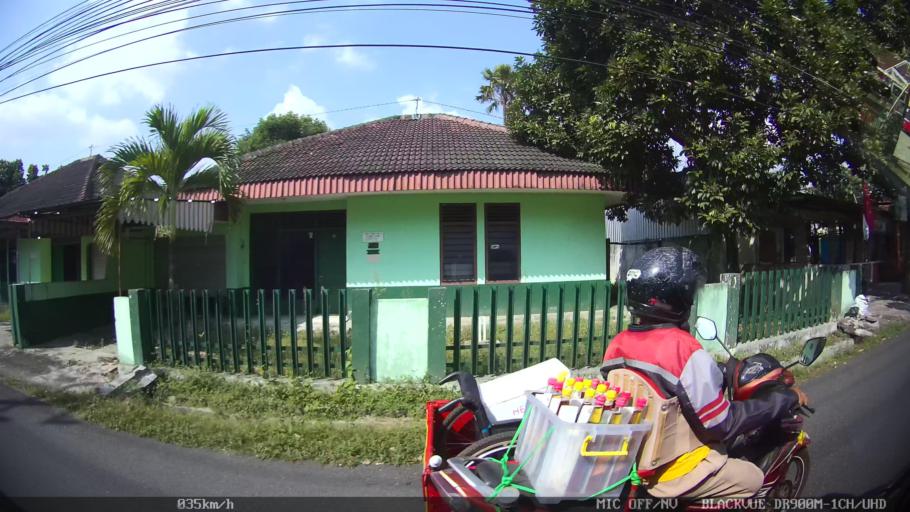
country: ID
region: Daerah Istimewa Yogyakarta
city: Melati
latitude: -7.7545
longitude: 110.3864
